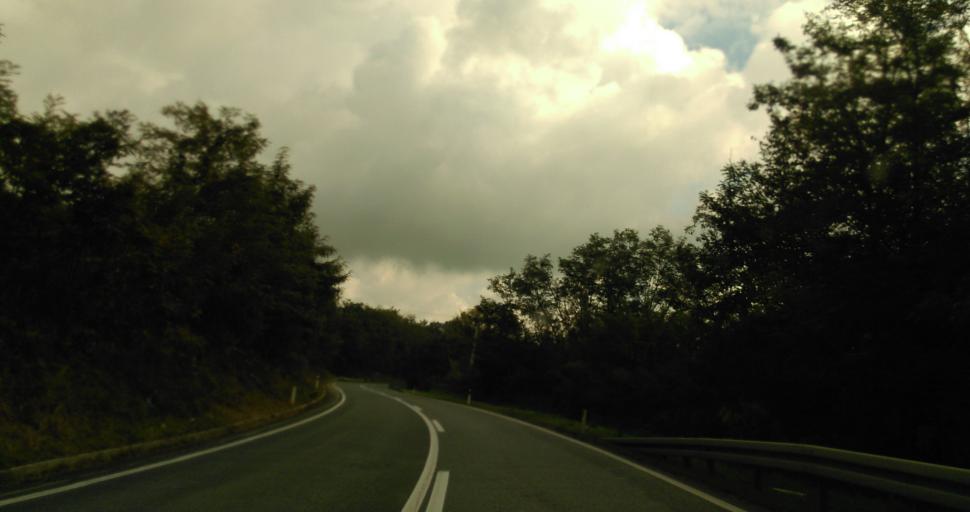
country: RS
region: Central Serbia
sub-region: Kolubarski Okrug
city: Ljig
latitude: 44.1951
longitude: 20.2967
